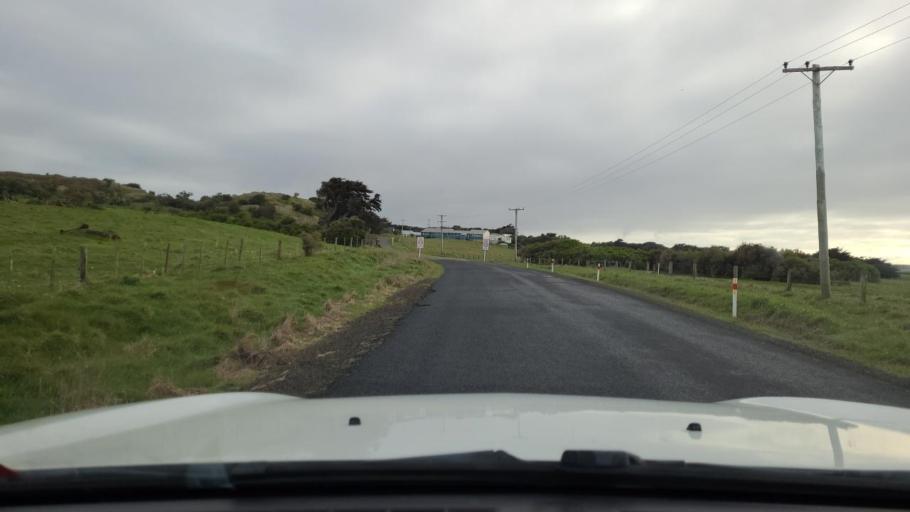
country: NZ
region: Chatham Islands
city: Waitangi
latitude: -43.9356
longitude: -176.5281
